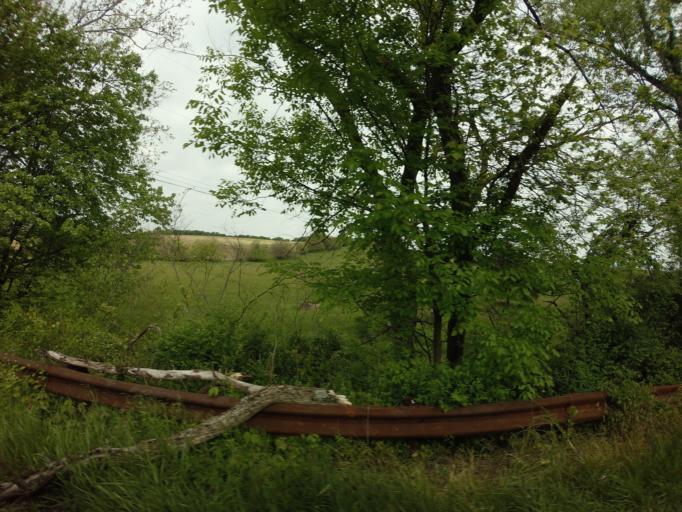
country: US
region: Maryland
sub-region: Montgomery County
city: Damascus
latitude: 39.3164
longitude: -77.2351
